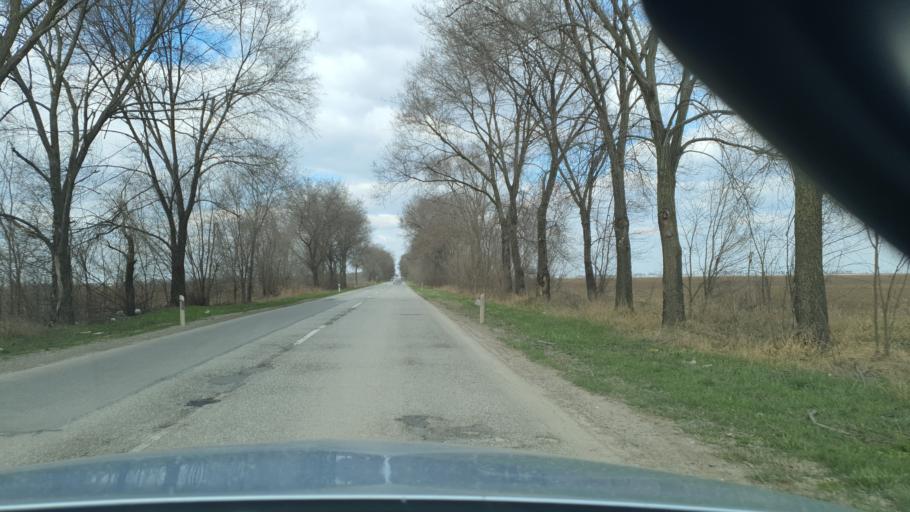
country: RS
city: Obrovac
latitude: 45.4355
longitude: 19.3765
